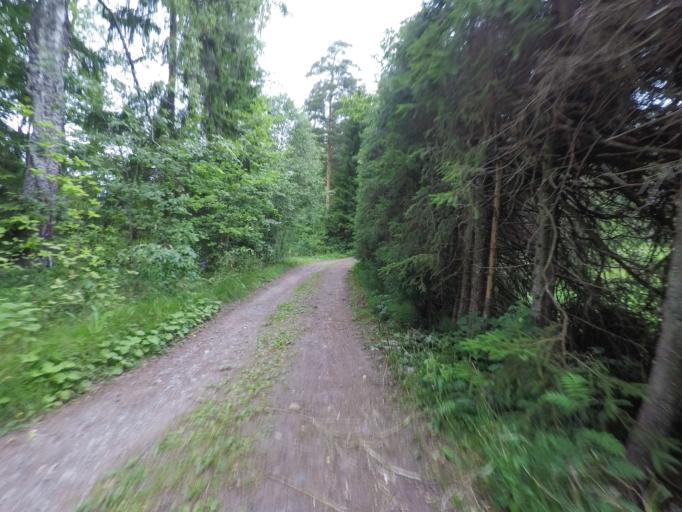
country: FI
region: Uusimaa
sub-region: Helsinki
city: Karjalohja
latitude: 60.2414
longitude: 23.6697
